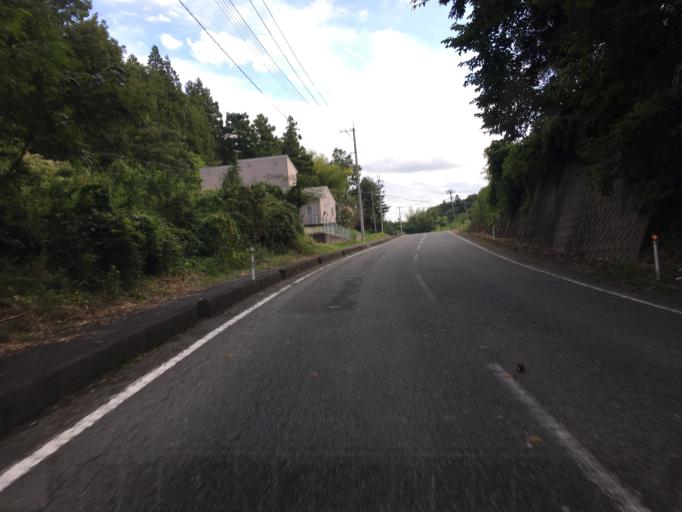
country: JP
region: Fukushima
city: Hobaramachi
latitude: 37.7905
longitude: 140.5424
